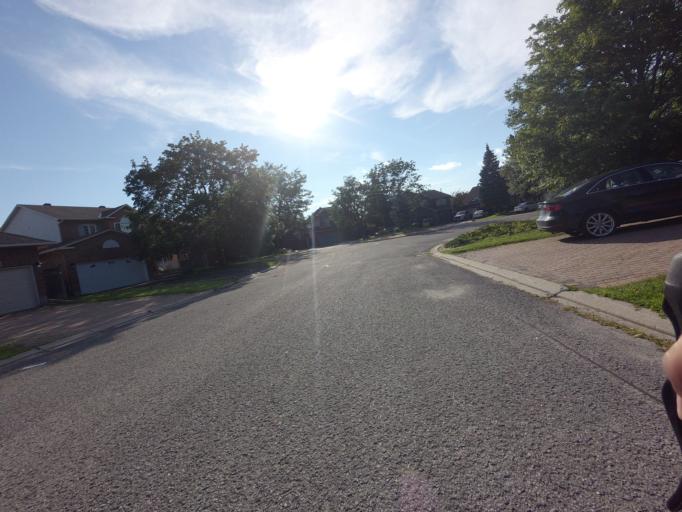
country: CA
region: Ontario
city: Bells Corners
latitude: 45.2946
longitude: -75.7357
